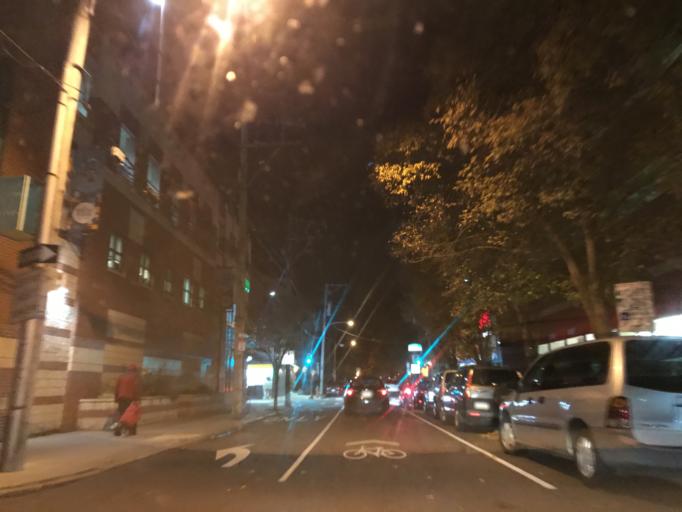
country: US
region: Pennsylvania
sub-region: Philadelphia County
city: Philadelphia
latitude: 39.9432
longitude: -75.1587
